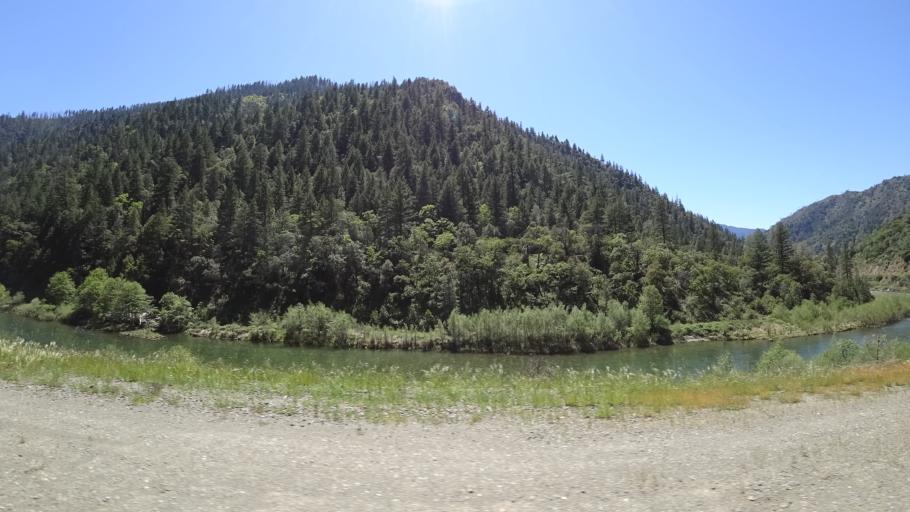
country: US
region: California
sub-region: Humboldt County
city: Willow Creek
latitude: 40.8002
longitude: -123.3881
